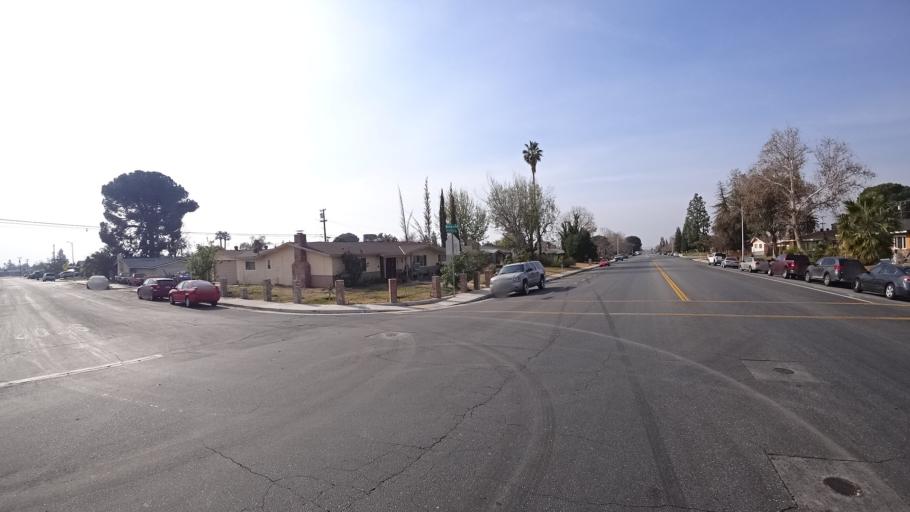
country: US
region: California
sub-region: Kern County
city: Oildale
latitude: 35.4050
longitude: -118.9545
